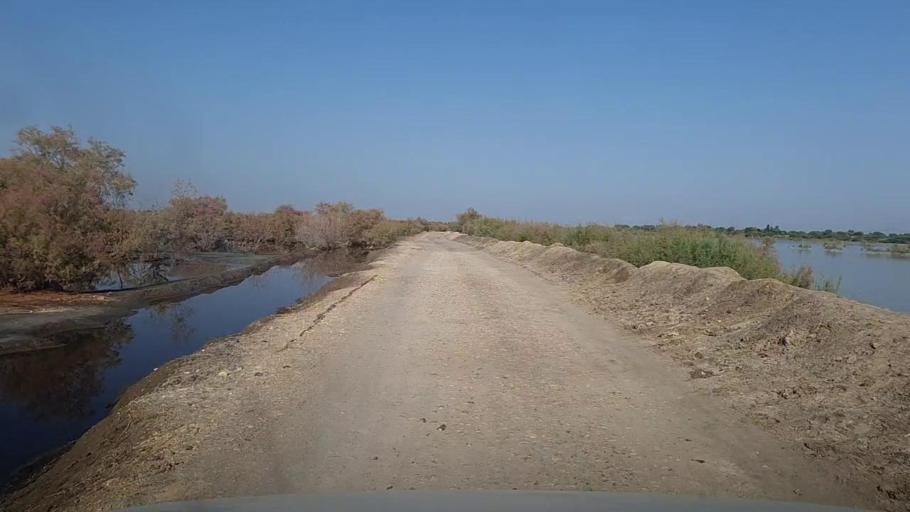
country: PK
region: Sindh
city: Kandhkot
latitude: 28.2808
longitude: 69.3259
